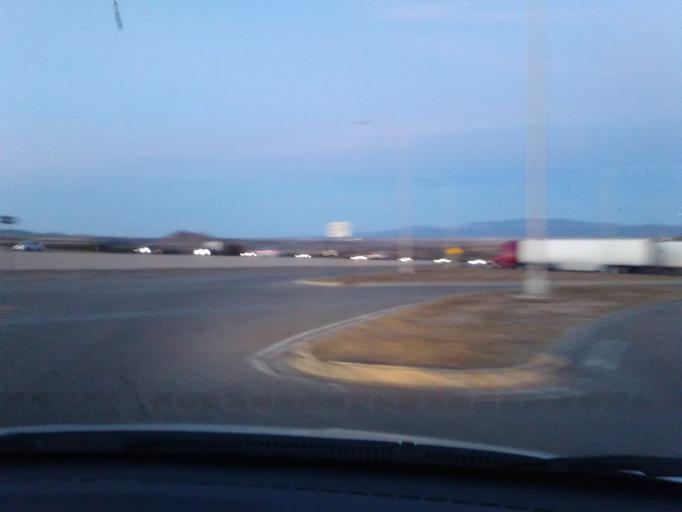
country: US
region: New Mexico
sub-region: Santa Fe County
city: La Cienega
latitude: 35.5277
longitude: -106.1562
